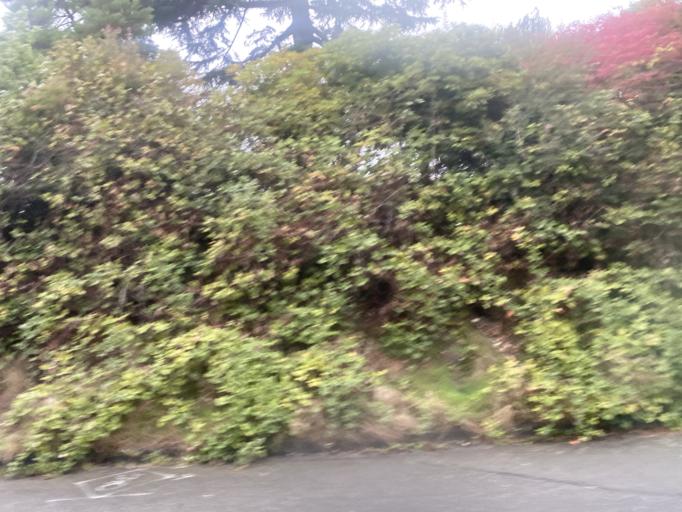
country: US
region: Washington
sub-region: King County
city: Seattle
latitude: 47.6452
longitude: -122.4141
